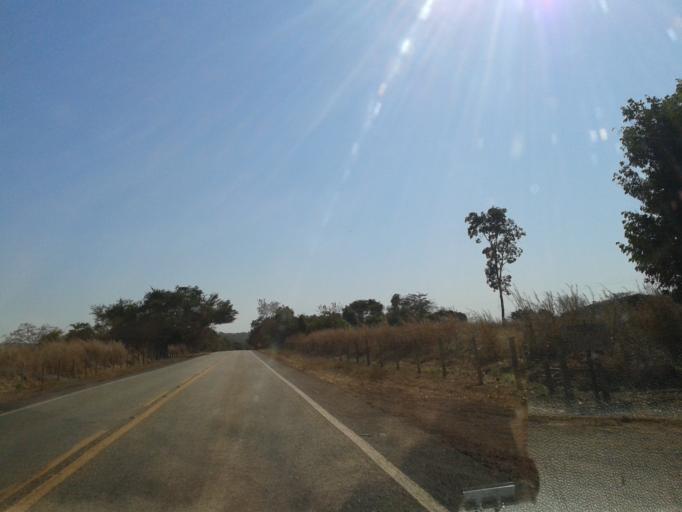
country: BR
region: Goias
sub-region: Mozarlandia
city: Mozarlandia
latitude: -14.6648
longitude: -50.5318
